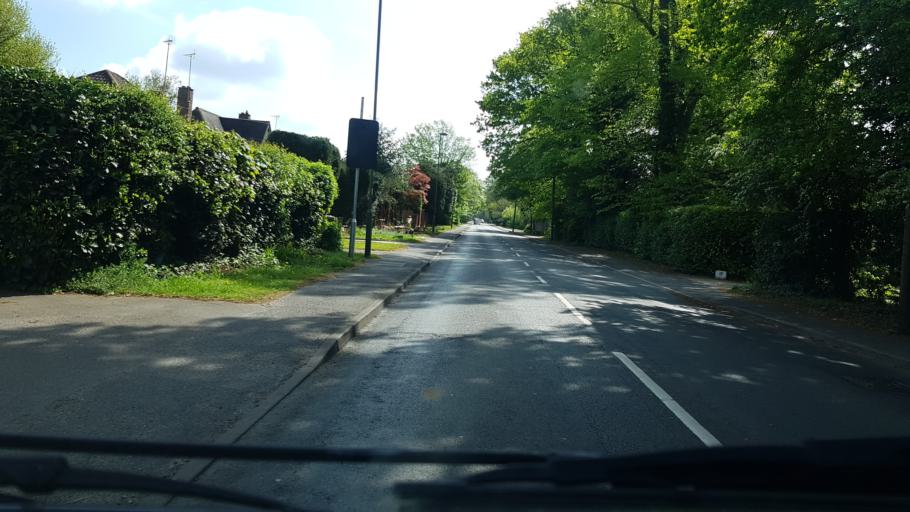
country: GB
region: England
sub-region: Surrey
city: Cobham
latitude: 51.3247
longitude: -0.3982
